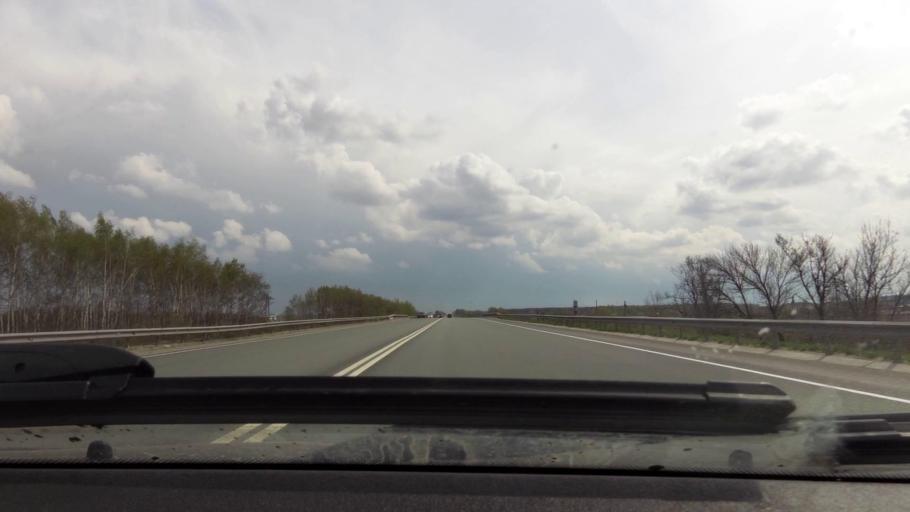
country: RU
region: Rjazan
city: Bagramovo
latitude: 54.7369
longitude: 39.4510
